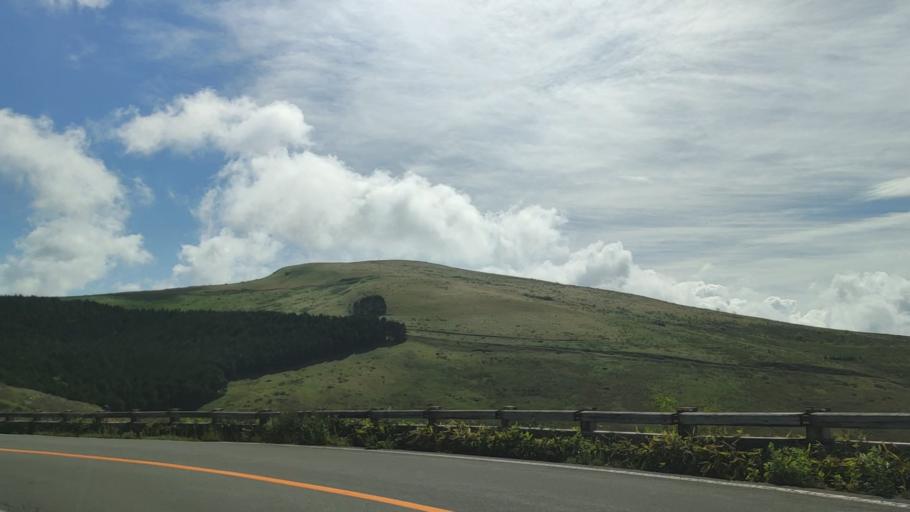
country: JP
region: Nagano
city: Suwa
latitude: 36.0989
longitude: 138.1816
